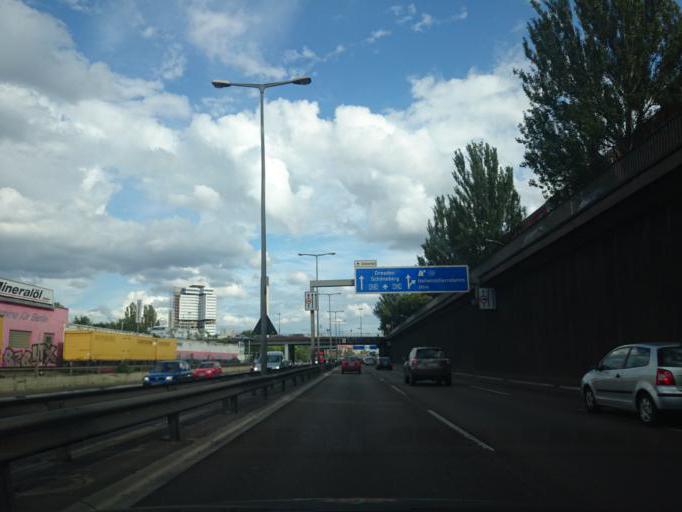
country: DE
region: Berlin
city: Halensee
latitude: 52.4927
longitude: 13.2928
